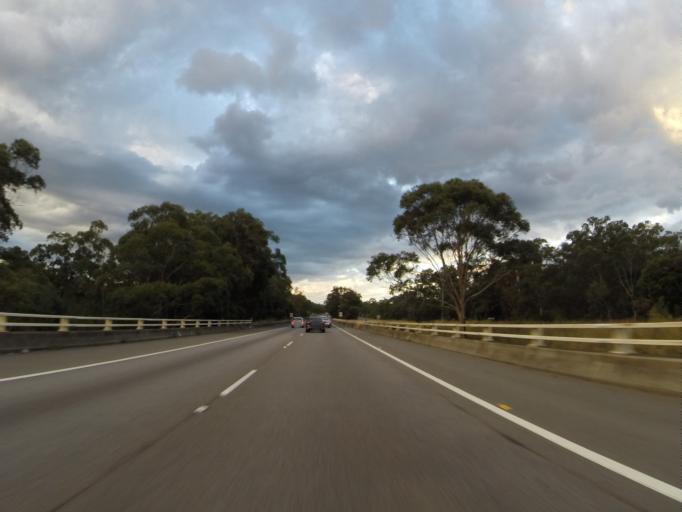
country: AU
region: New South Wales
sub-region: Wollondilly
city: Douglas Park
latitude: -34.1912
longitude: 150.7128
